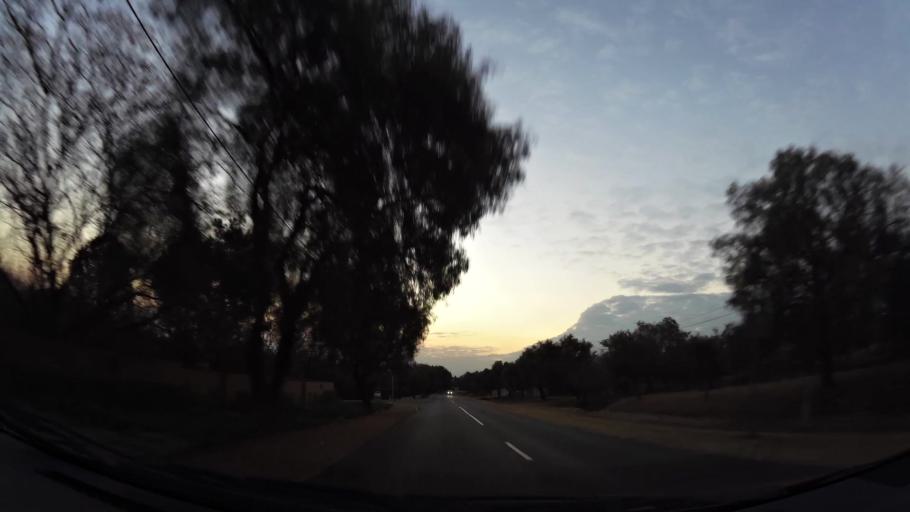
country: ZA
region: Gauteng
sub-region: City of Johannesburg Metropolitan Municipality
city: Midrand
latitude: -25.9719
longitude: 28.0670
